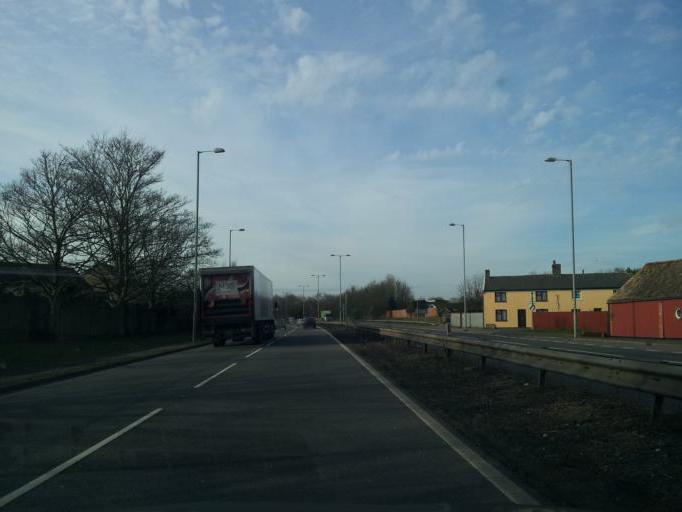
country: GB
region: England
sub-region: Cambridgeshire
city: Buckden
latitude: 52.2987
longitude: -0.2512
